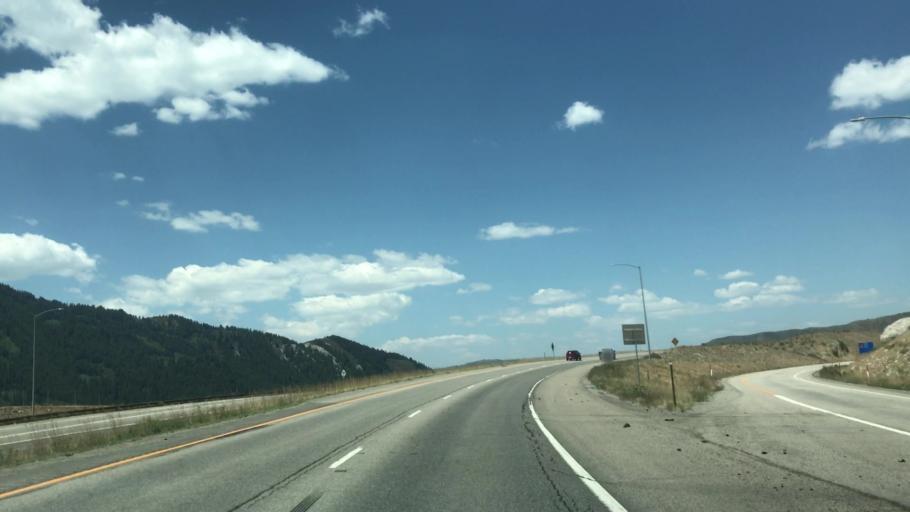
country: US
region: Colorado
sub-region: Eagle County
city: Avon
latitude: 39.6252
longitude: -106.4911
